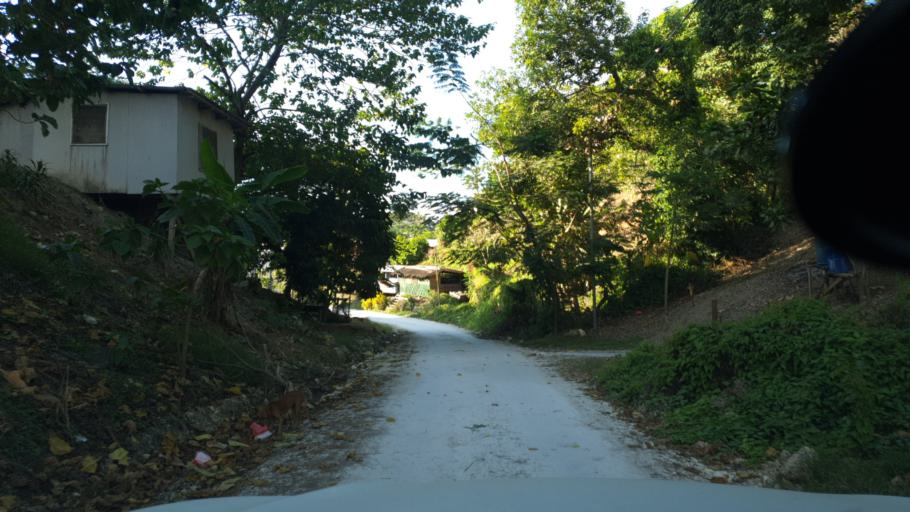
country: SB
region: Guadalcanal
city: Honiara
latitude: -9.4303
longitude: 160.0068
